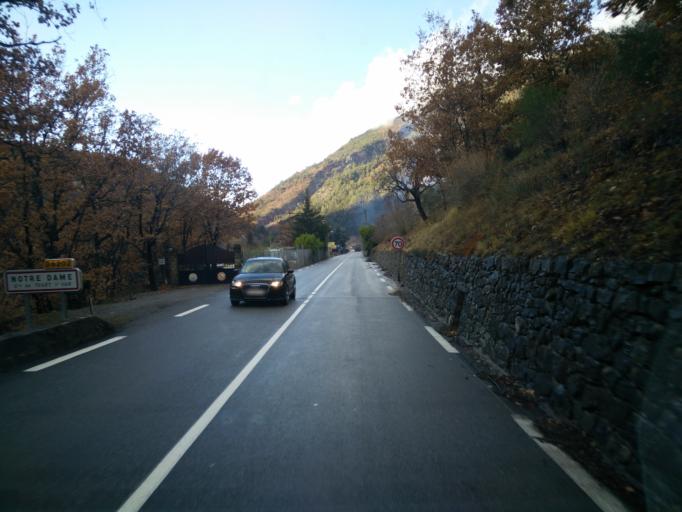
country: FR
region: Provence-Alpes-Cote d'Azur
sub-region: Departement des Alpes-Maritimes
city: Puget-Theniers
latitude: 43.9471
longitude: 6.9953
